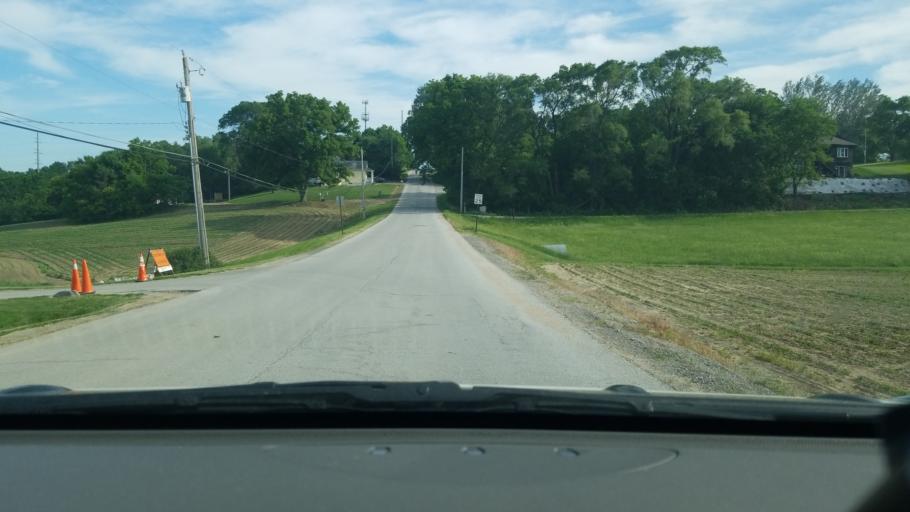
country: US
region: Nebraska
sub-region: Sarpy County
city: Offutt Air Force Base
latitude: 41.1725
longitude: -95.9336
